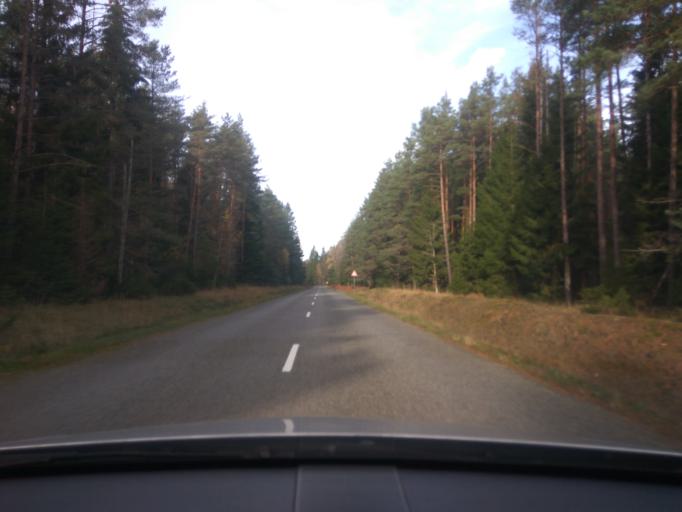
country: LV
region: Alsunga
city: Alsunga
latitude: 56.9963
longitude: 21.4905
